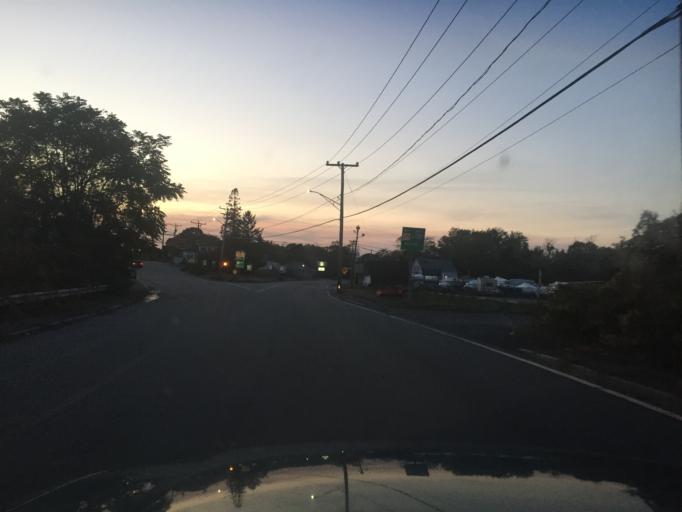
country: US
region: Massachusetts
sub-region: Plymouth County
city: Onset
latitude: 41.7627
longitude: -70.6763
